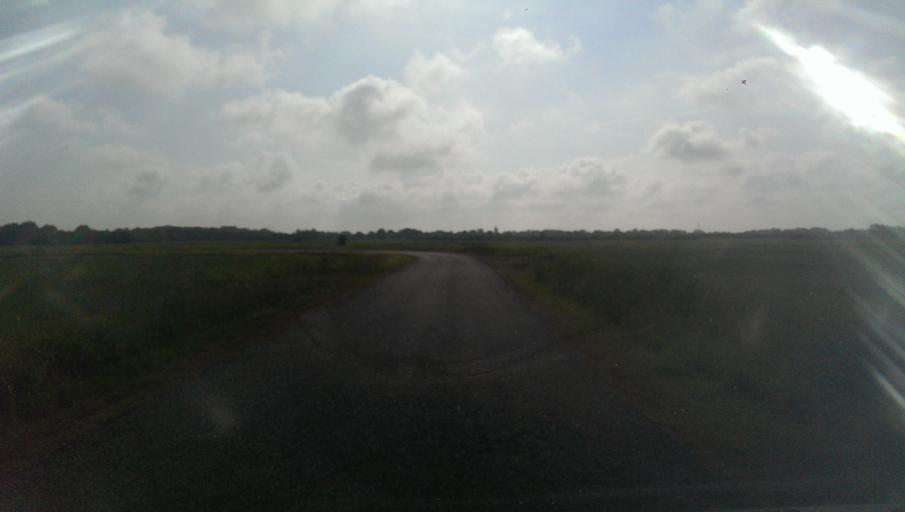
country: DK
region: South Denmark
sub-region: Esbjerg Kommune
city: Tjaereborg
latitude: 55.4322
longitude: 8.6269
